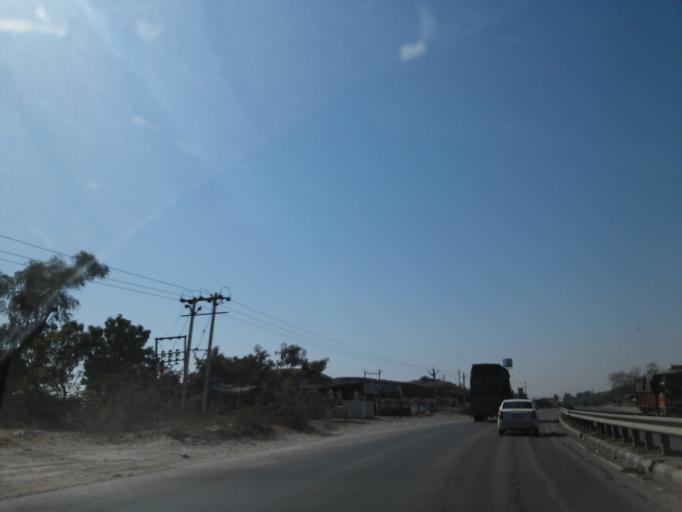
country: IN
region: Rajasthan
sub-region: Dungarpur
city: Dungarpur
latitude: 24.0823
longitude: 73.6867
